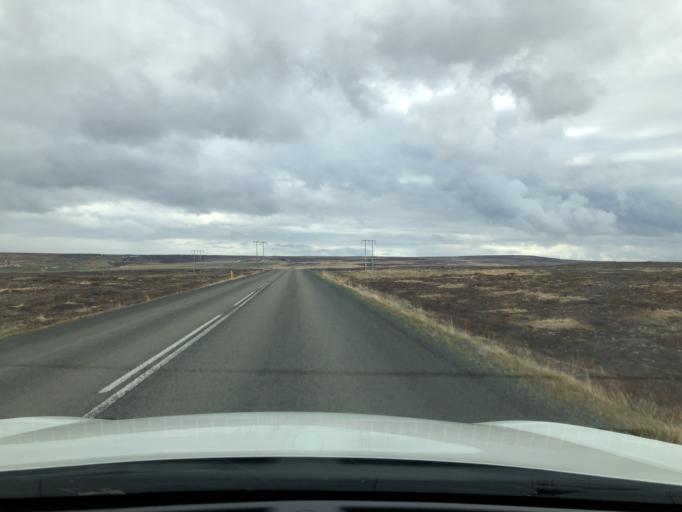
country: IS
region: Northeast
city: Laugar
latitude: 65.6985
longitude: -17.5902
